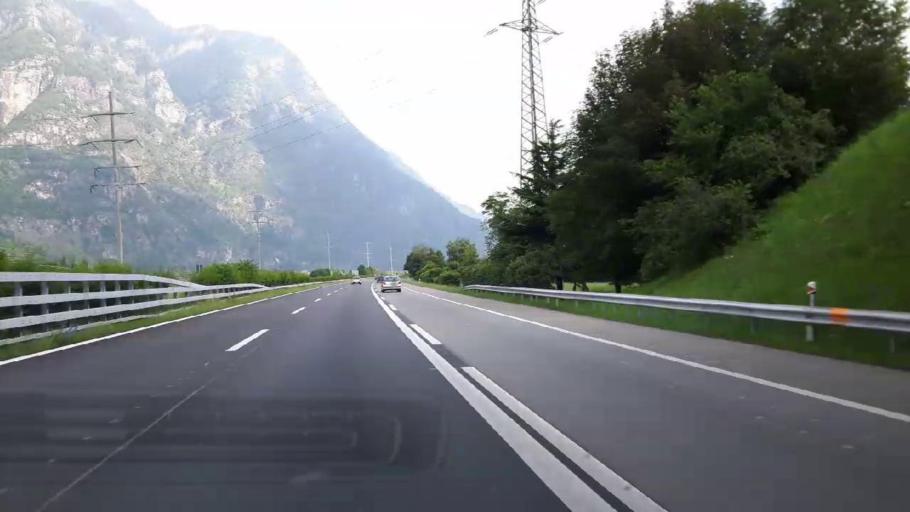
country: CH
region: Ticino
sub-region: Riviera District
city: Biasca
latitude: 46.3552
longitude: 8.9573
